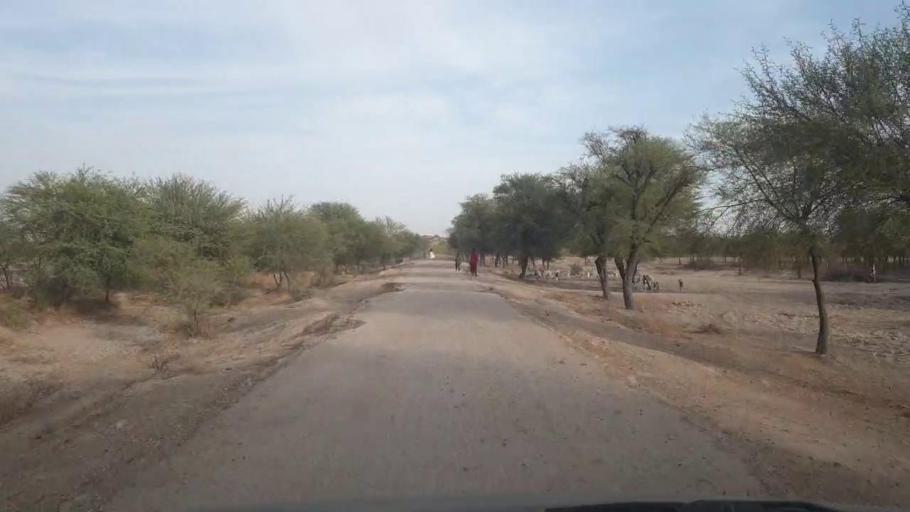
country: PK
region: Sindh
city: Nabisar
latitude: 25.0974
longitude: 69.6533
